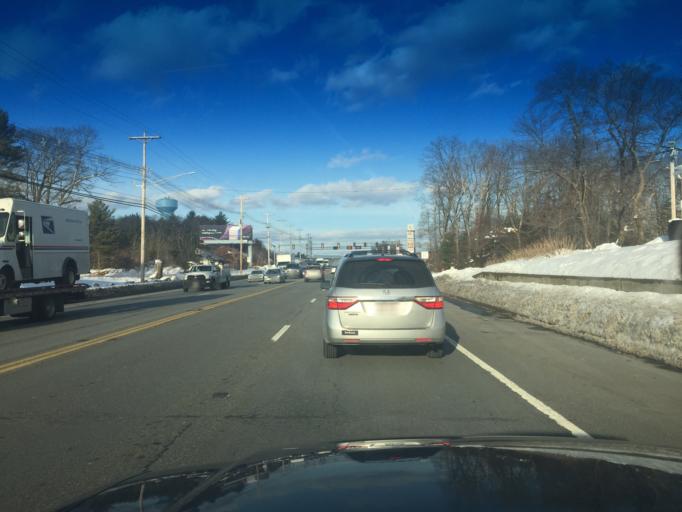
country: US
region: Massachusetts
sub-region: Norfolk County
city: Foxborough
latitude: 42.0849
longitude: -71.2765
